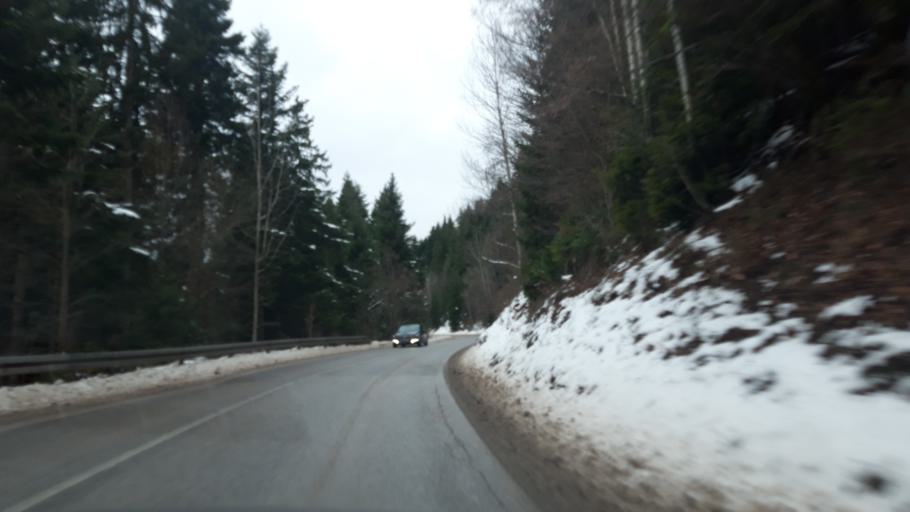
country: BA
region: Republika Srpska
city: Koran
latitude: 43.8038
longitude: 18.5514
